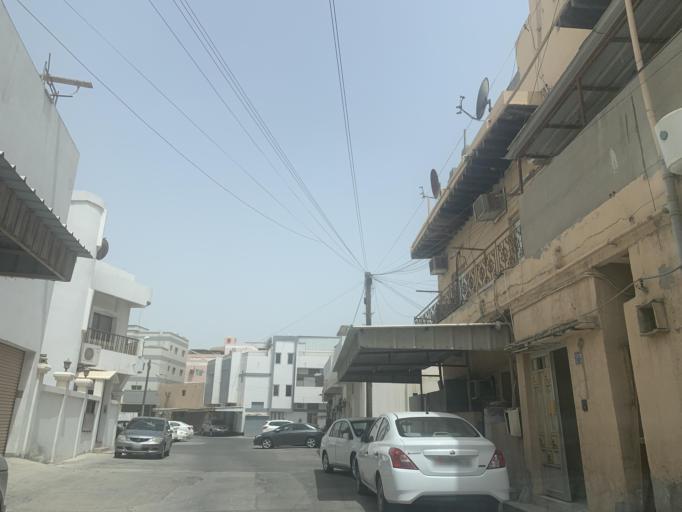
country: BH
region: Manama
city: Jidd Hafs
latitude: 26.2108
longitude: 50.5455
